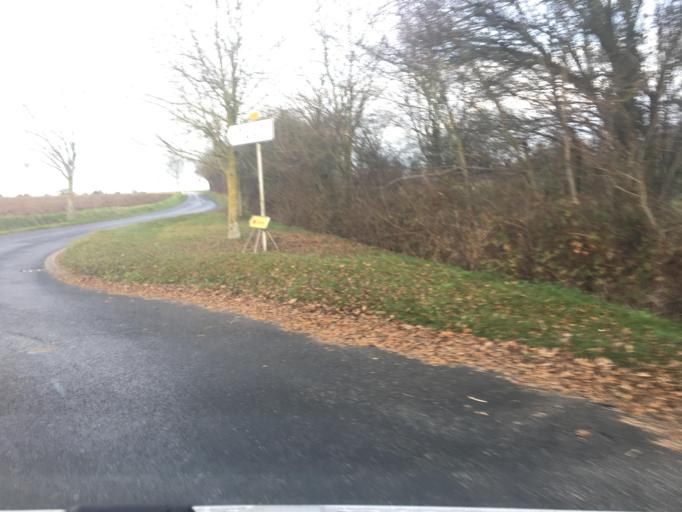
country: FR
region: Lower Normandy
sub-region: Departement du Calvados
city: Ver-sur-Mer
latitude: 49.3182
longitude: -0.5518
